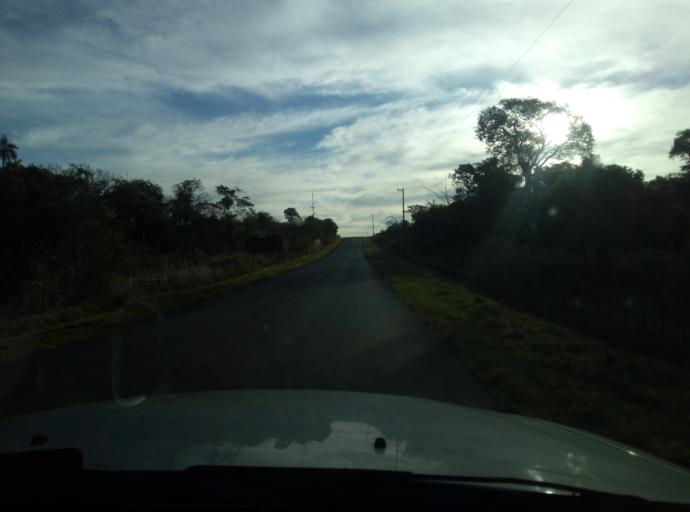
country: PY
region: Caaguazu
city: Carayao
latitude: -25.1538
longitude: -56.3205
